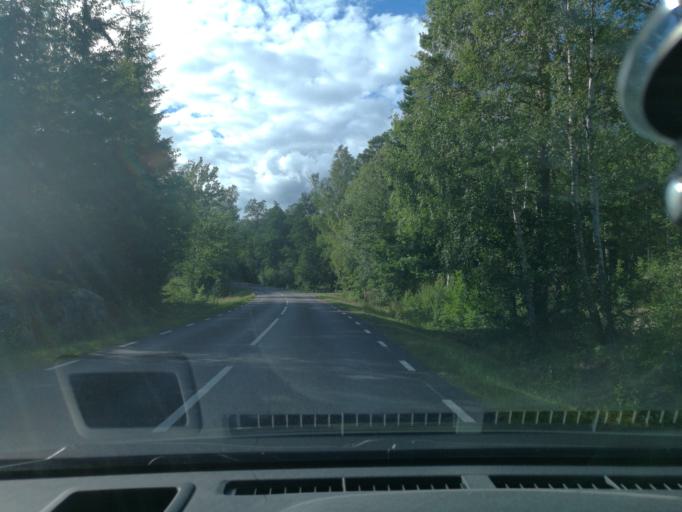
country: SE
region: Kronoberg
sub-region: Vaxjo Kommun
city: Braas
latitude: 57.0623
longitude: 15.0311
